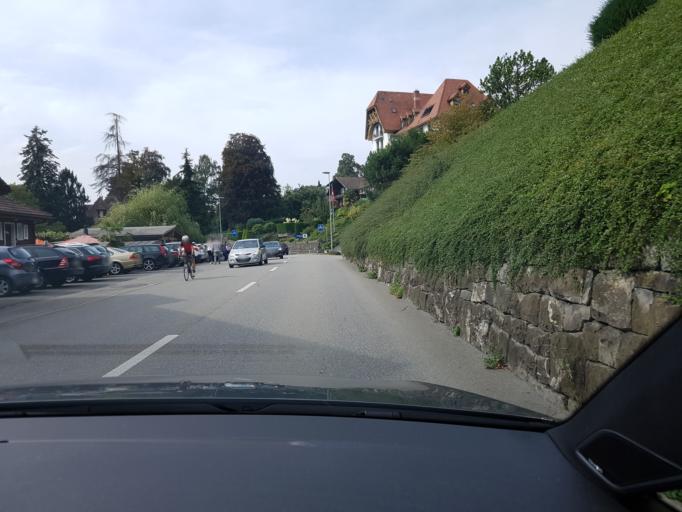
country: CH
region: Bern
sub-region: Thun District
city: Sigriswil
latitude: 46.7159
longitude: 7.6922
